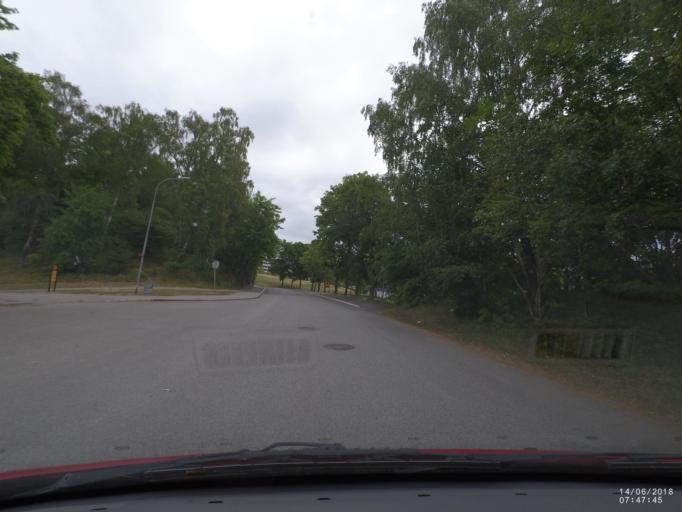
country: SE
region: Soedermanland
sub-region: Nykopings Kommun
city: Nykoping
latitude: 58.7656
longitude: 17.0124
